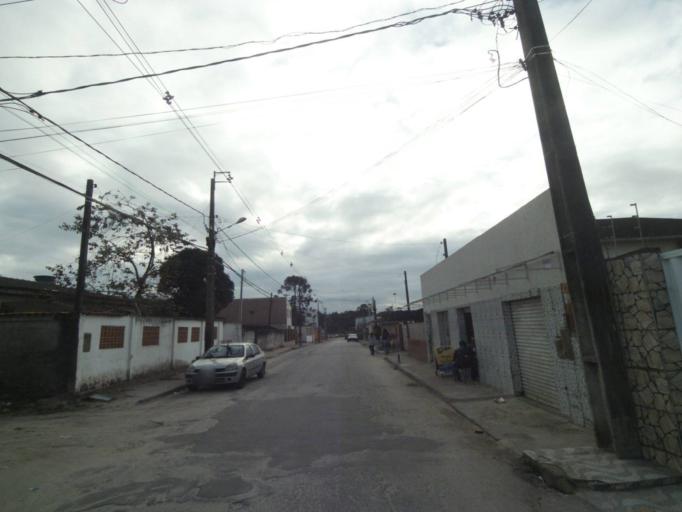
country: BR
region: Parana
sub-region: Paranagua
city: Paranagua
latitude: -25.5315
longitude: -48.5473
